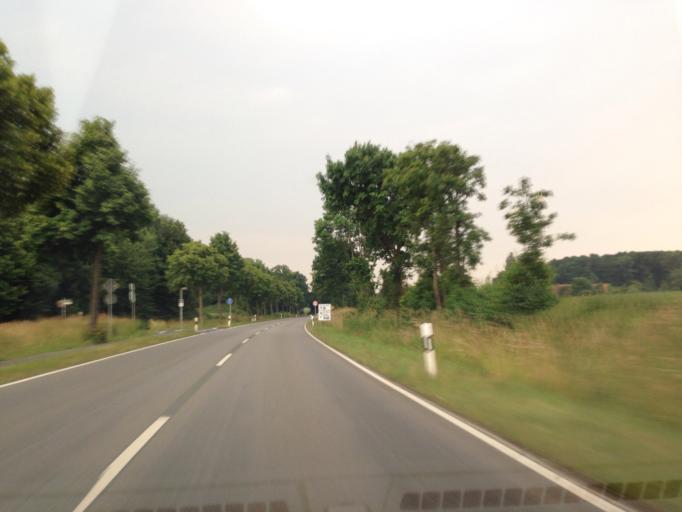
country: DE
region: North Rhine-Westphalia
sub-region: Regierungsbezirk Munster
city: Havixbeck
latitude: 51.9439
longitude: 7.4373
